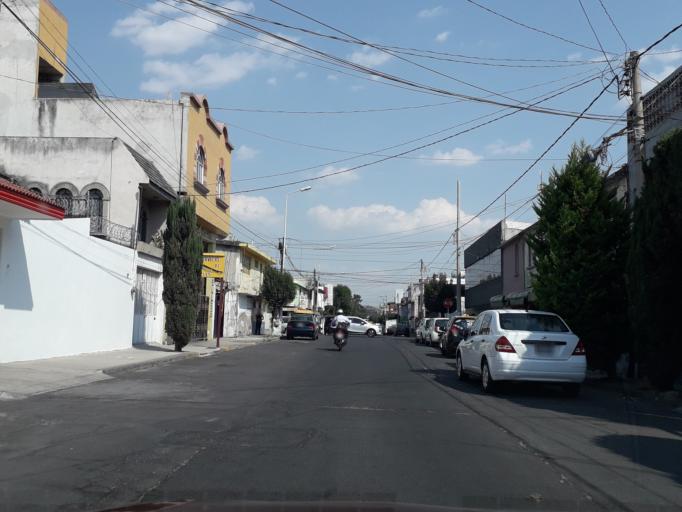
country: MX
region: Puebla
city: Puebla
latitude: 19.0453
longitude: -98.2281
